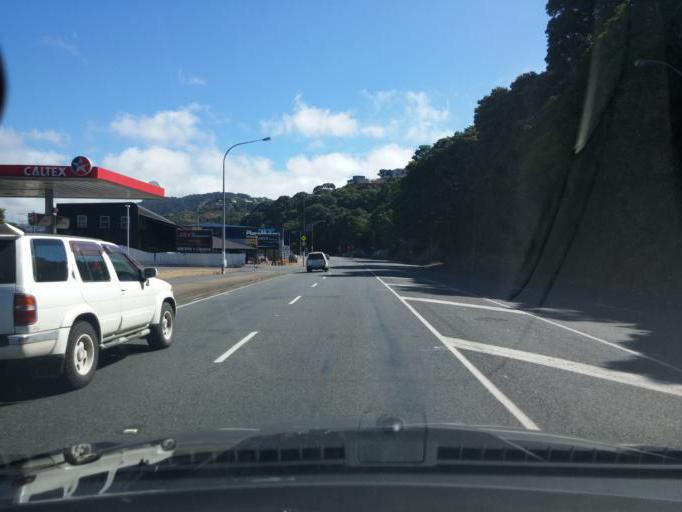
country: NZ
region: Wellington
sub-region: Wellington City
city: Wellington
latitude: -41.2551
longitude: 174.7986
